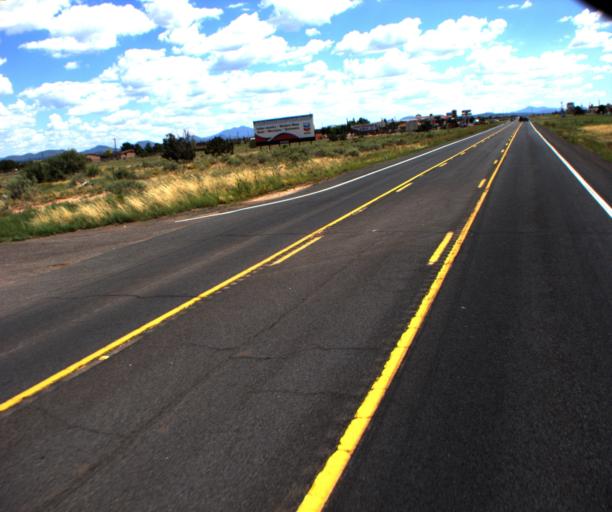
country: US
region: Arizona
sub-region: Coconino County
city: Grand Canyon Village
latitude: 35.6575
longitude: -112.1388
